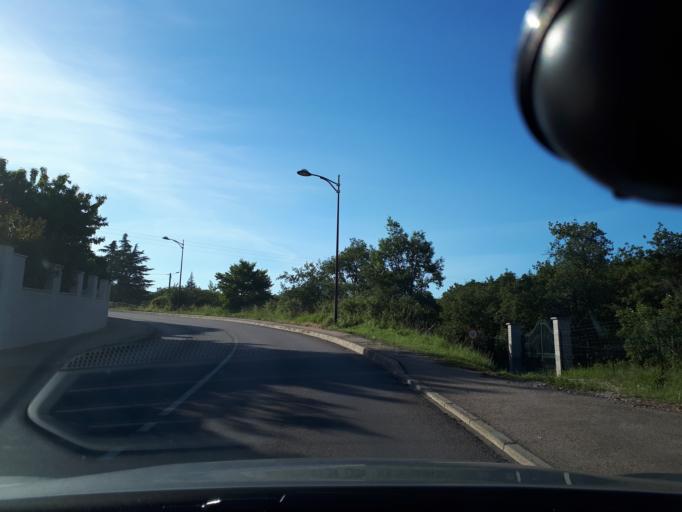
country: FR
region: Rhone-Alpes
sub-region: Departement de la Loire
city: Chateauneuf
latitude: 45.5435
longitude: 4.6394
